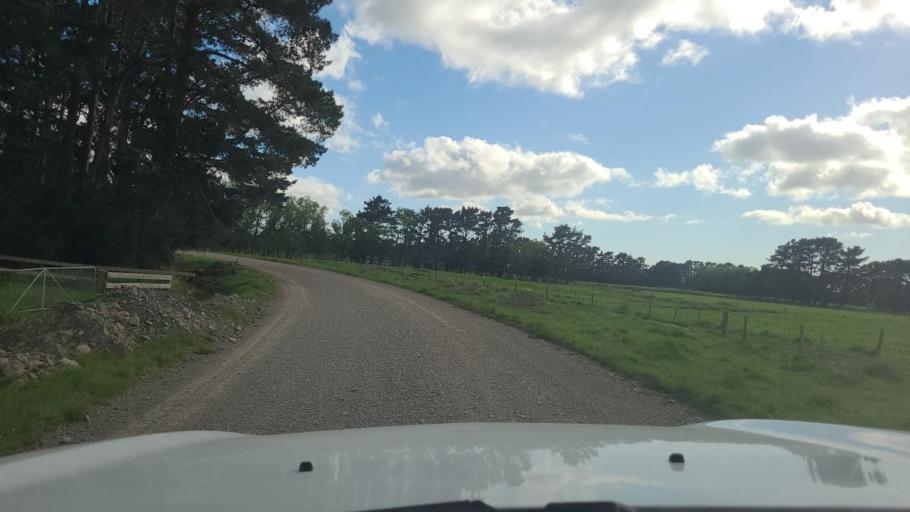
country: NZ
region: Wellington
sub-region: Upper Hutt City
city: Upper Hutt
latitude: -41.3062
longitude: 175.2245
